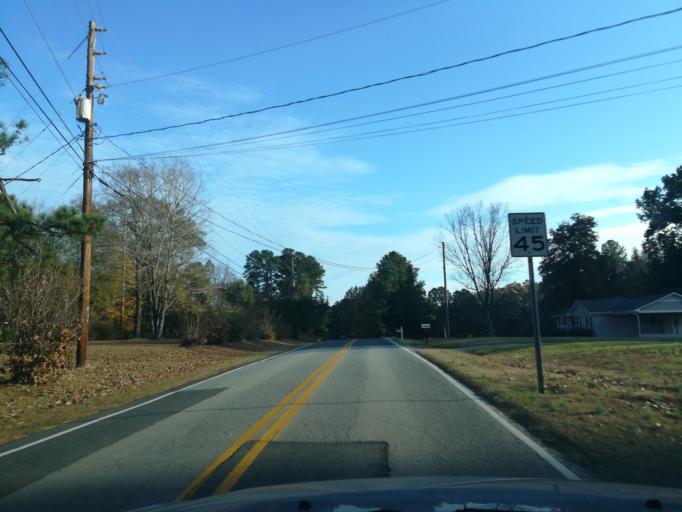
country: US
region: North Carolina
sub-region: Orange County
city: Chapel Hill
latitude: 35.9620
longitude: -79.0000
